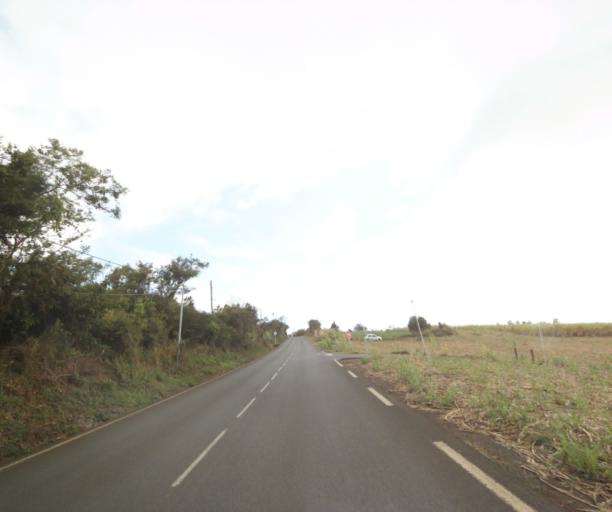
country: RE
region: Reunion
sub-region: Reunion
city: Trois-Bassins
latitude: -21.0661
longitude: 55.2787
